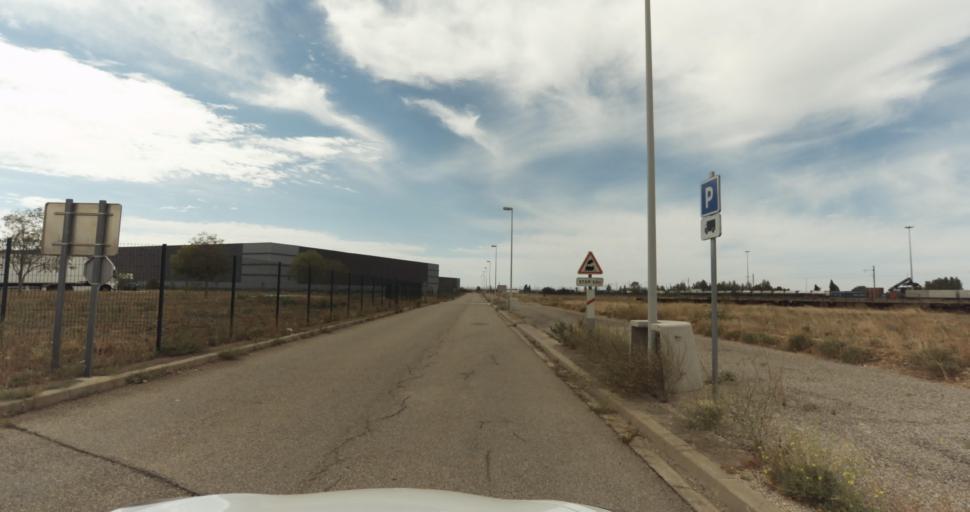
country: FR
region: Provence-Alpes-Cote d'Azur
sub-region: Departement des Bouches-du-Rhone
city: Miramas
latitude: 43.6068
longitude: 4.9922
